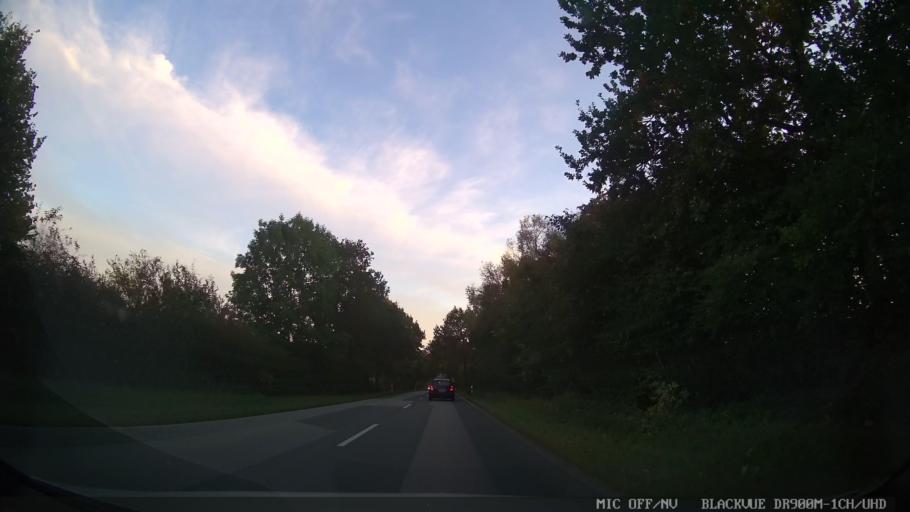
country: DE
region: Schleswig-Holstein
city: Susel
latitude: 54.0295
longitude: 10.6828
